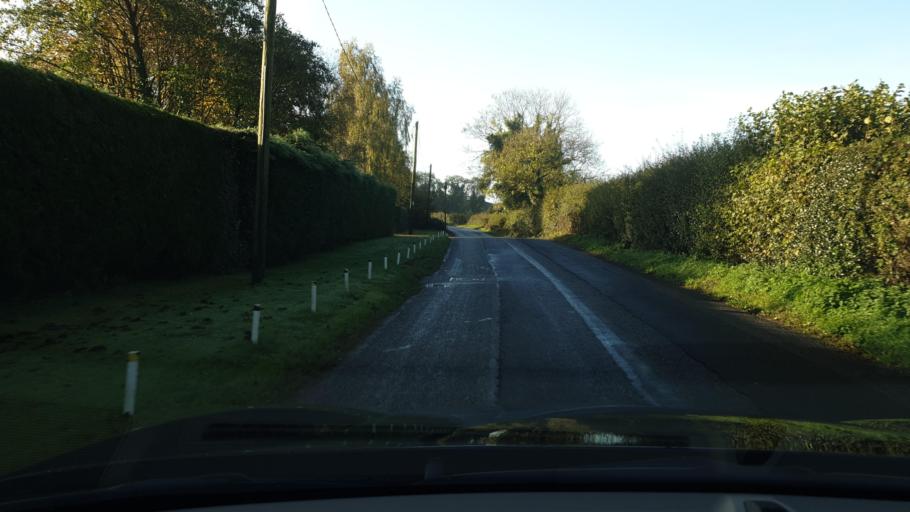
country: IE
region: Leinster
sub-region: An Mhi
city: Ashbourne
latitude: 53.4672
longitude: -6.3784
